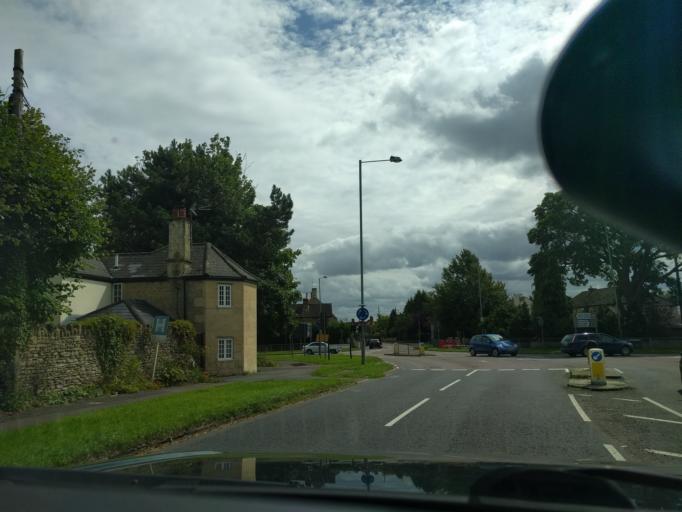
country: GB
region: England
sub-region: Wiltshire
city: Chippenham
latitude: 51.4663
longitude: -2.1366
